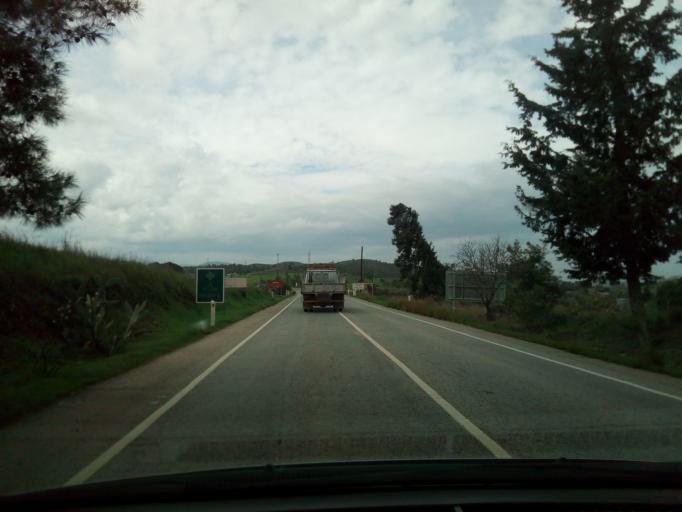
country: CY
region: Lefkosia
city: Kakopetria
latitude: 35.0706
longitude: 32.9286
